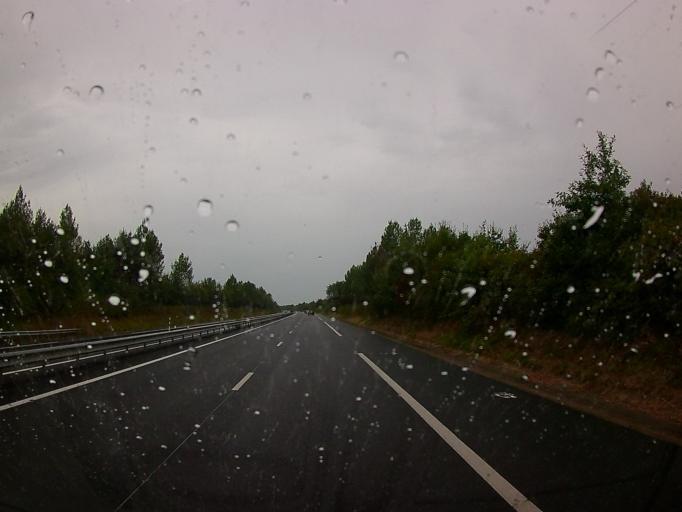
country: FR
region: Aquitaine
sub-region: Departement de la Dordogne
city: Saint-Medard-de-Mussidan
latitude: 45.0093
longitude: 0.3112
